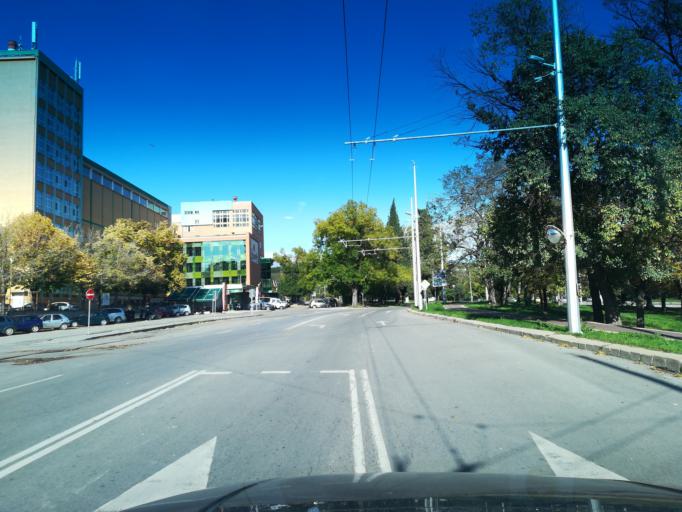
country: BG
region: Stara Zagora
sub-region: Obshtina Stara Zagora
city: Stara Zagora
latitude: 42.4422
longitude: 25.6337
